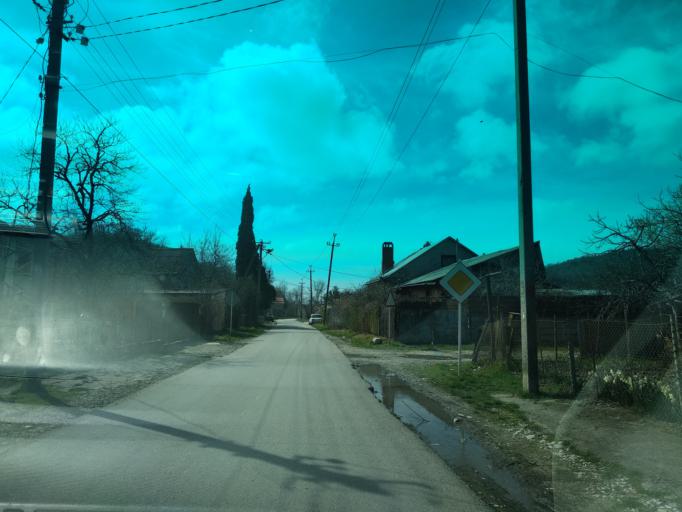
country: RU
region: Krasnodarskiy
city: Shepsi
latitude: 44.0495
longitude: 39.1597
